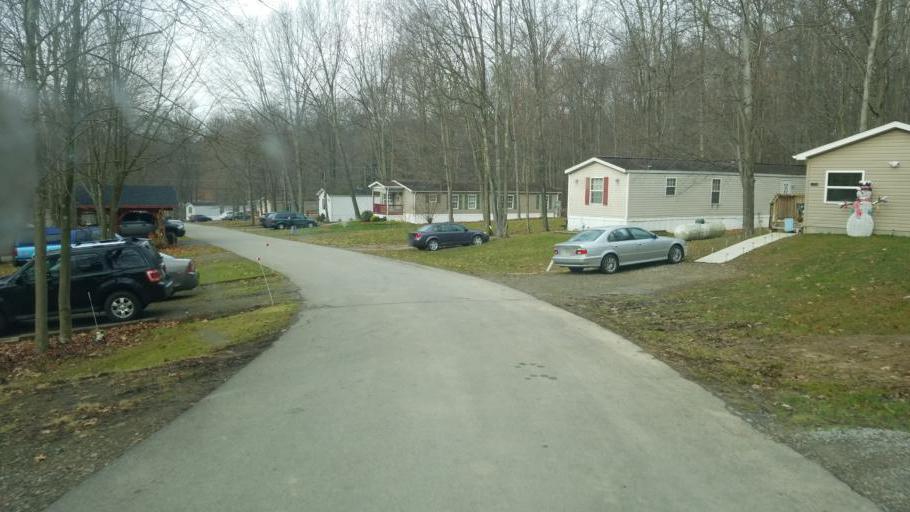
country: US
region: Pennsylvania
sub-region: Crawford County
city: Meadville
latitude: 41.5630
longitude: -80.1869
